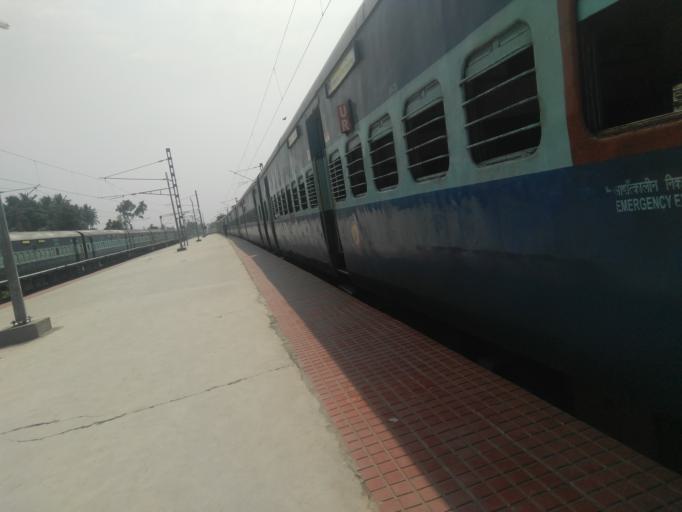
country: IN
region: Tamil Nadu
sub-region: Coimbatore
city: Mettupalayam
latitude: 11.2955
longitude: 76.9363
